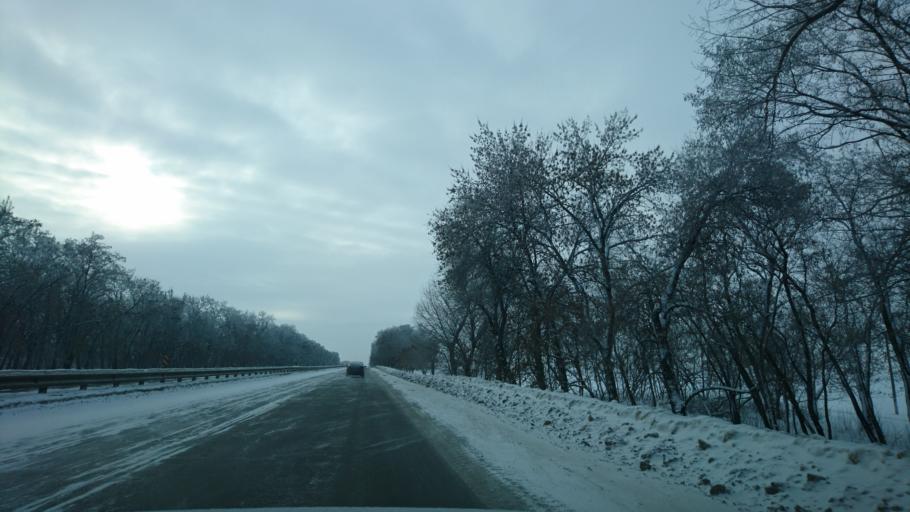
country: RU
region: Belgorod
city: Mayskiy
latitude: 50.4800
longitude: 36.4060
